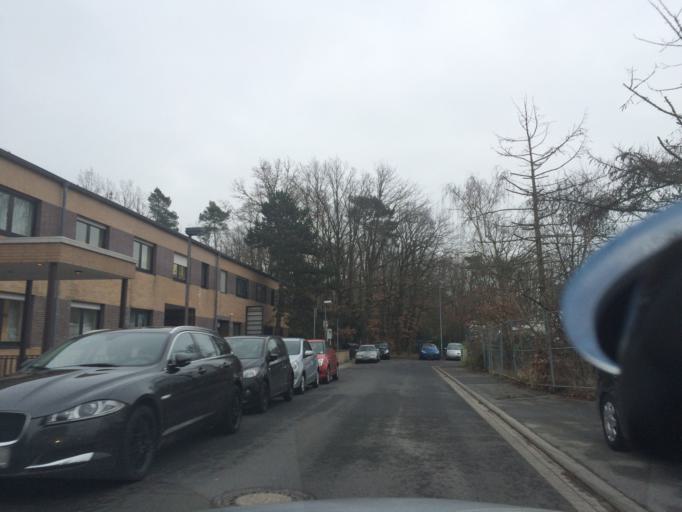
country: DE
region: Hesse
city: Niederrad
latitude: 50.0383
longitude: 8.6087
